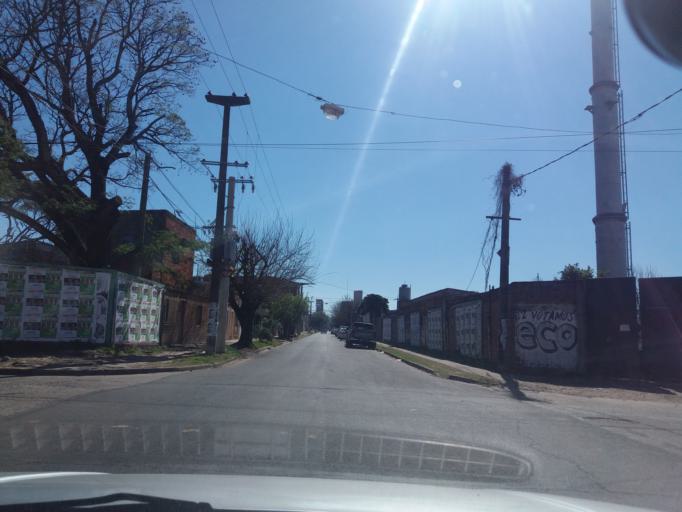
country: AR
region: Corrientes
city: Corrientes
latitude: -27.4809
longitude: -58.8438
